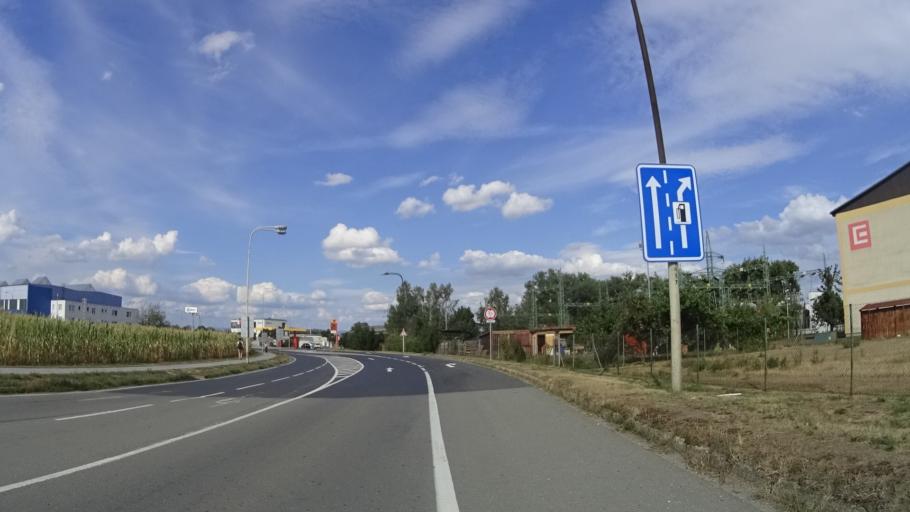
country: CZ
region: Olomoucky
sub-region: Okres Sumperk
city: Mohelnice
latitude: 49.7734
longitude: 16.9404
